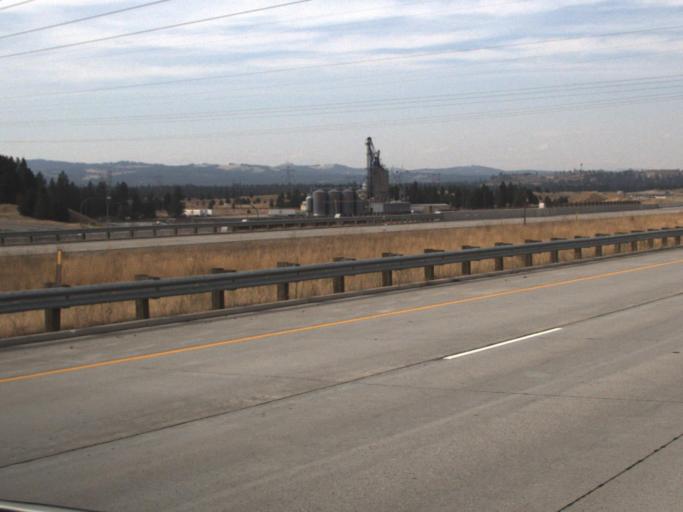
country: US
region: Washington
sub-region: Spokane County
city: Mead
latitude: 47.7512
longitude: -117.3593
